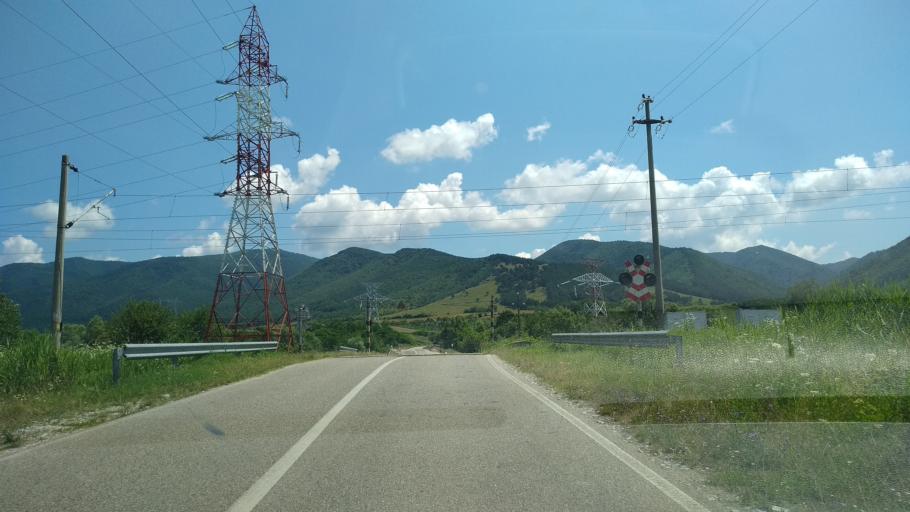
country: RO
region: Hunedoara
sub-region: Comuna Santamaria-Orlea
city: Santamaria-Orlea
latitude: 45.5893
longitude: 22.9876
